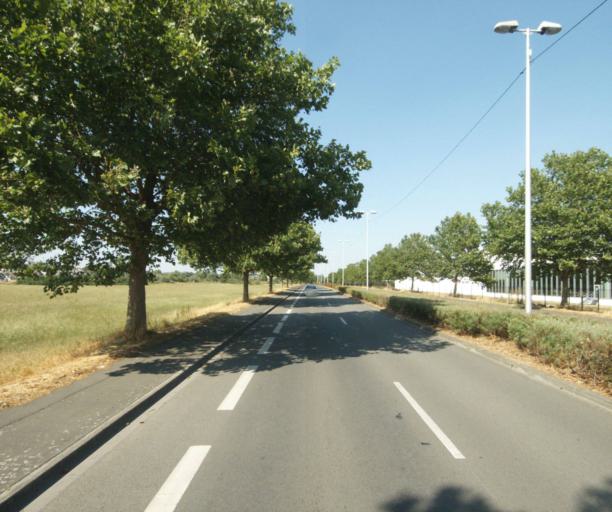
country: FR
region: Nord-Pas-de-Calais
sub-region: Departement du Nord
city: Wattrelos
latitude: 50.7163
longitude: 3.2034
